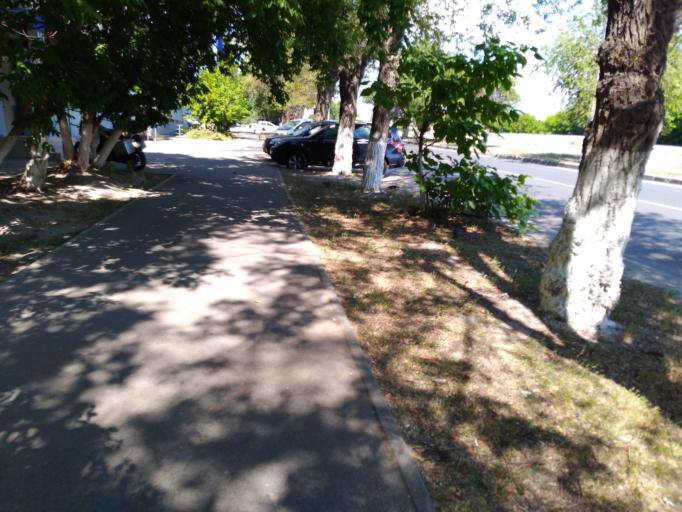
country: RU
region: Volgograd
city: Volgograd
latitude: 48.7170
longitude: 44.5165
